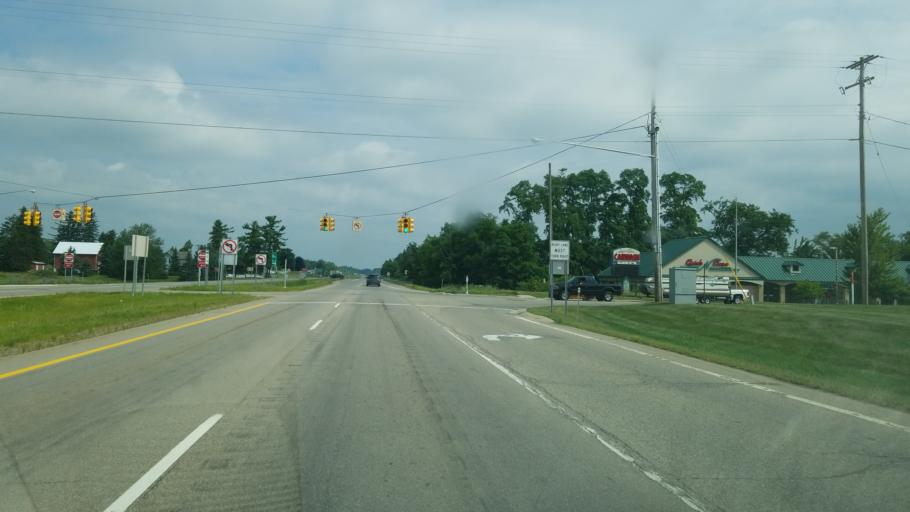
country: US
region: Michigan
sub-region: Kent County
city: Comstock Park
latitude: 43.0721
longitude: -85.6899
